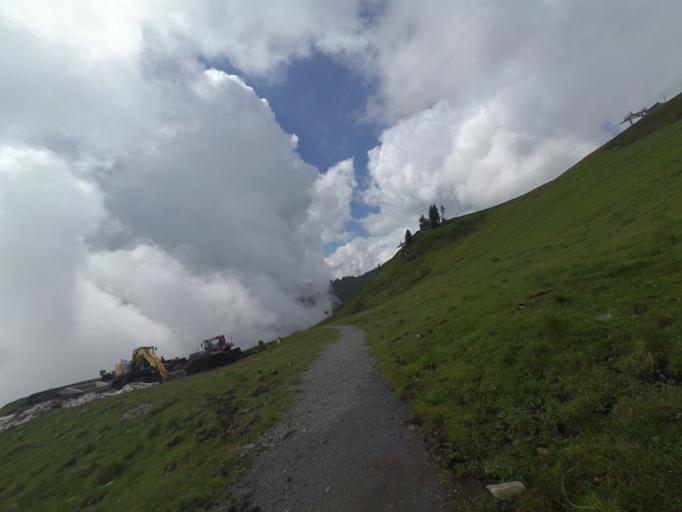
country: AT
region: Salzburg
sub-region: Politischer Bezirk Zell am See
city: Viehhofen
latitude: 47.4064
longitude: 12.7105
